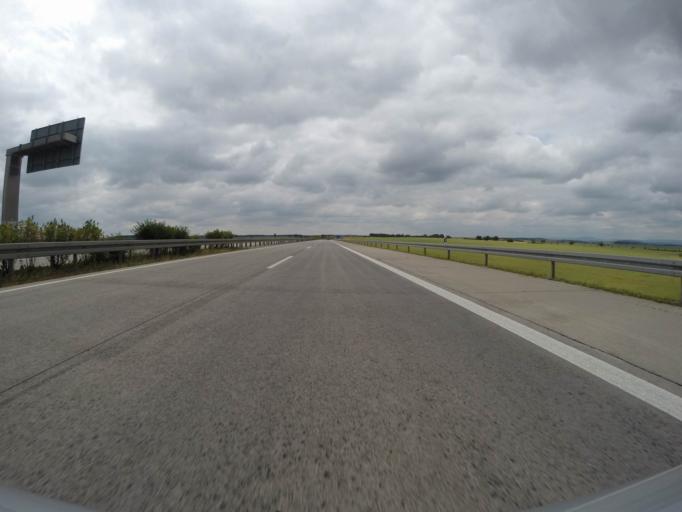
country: DE
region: Thuringia
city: Wolfershausen
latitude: 50.4454
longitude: 10.4428
